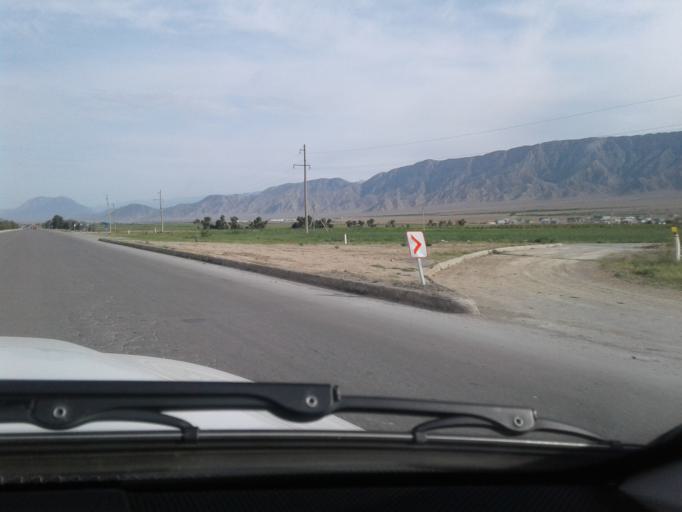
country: TM
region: Ahal
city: Arcabil
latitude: 38.2087
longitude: 57.8159
